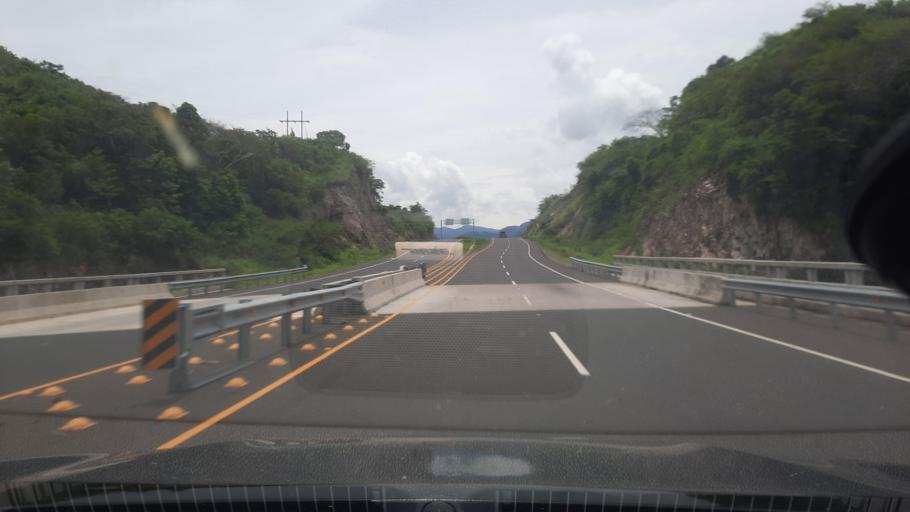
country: HN
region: Valle
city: Aramecina
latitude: 13.6907
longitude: -87.7189
